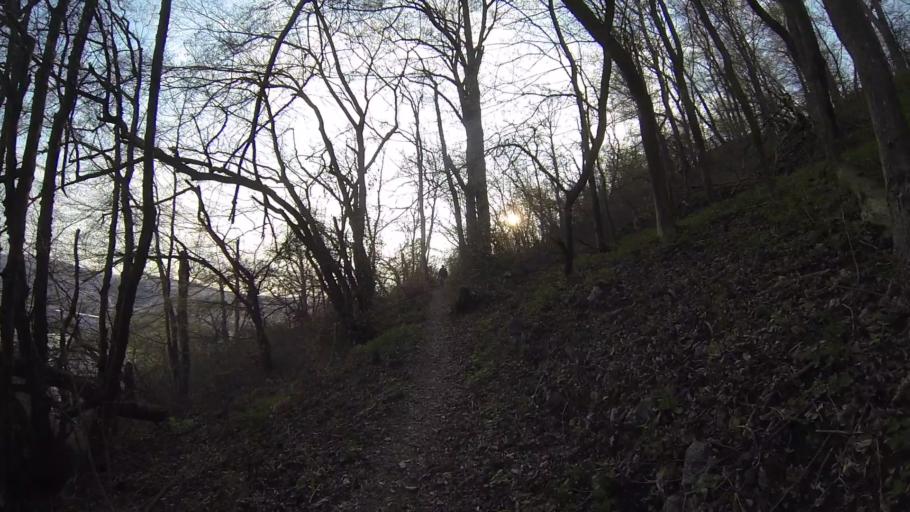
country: DE
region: Baden-Wuerttemberg
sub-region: Regierungsbezirk Stuttgart
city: Heidenheim an der Brenz
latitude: 48.6828
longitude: 10.1603
